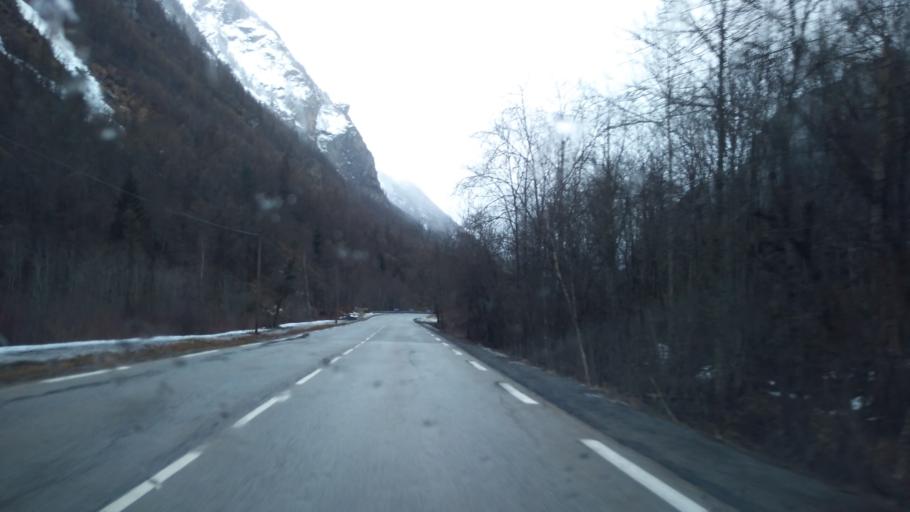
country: FR
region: Rhone-Alpes
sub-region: Departement de l'Isere
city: Mont-de-Lans
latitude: 45.0375
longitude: 6.1975
